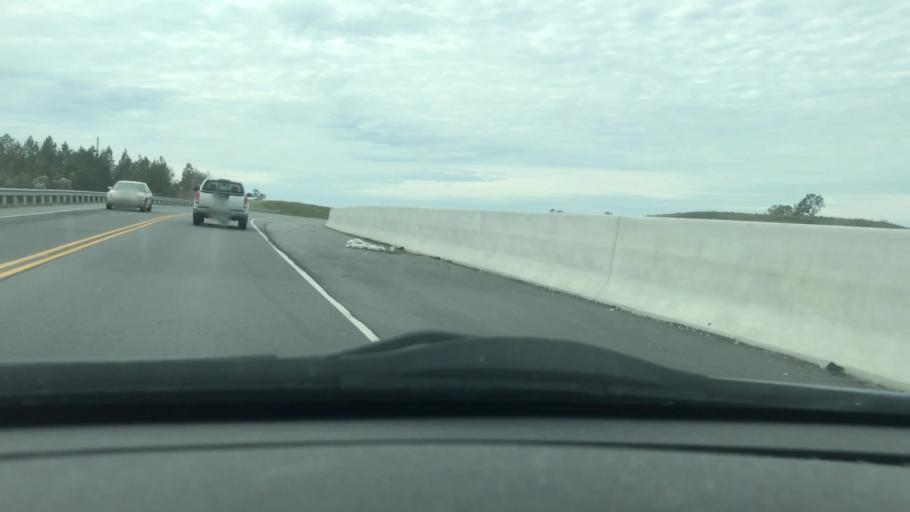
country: US
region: North Carolina
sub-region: Randolph County
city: Asheboro
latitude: 35.6974
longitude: -79.8684
